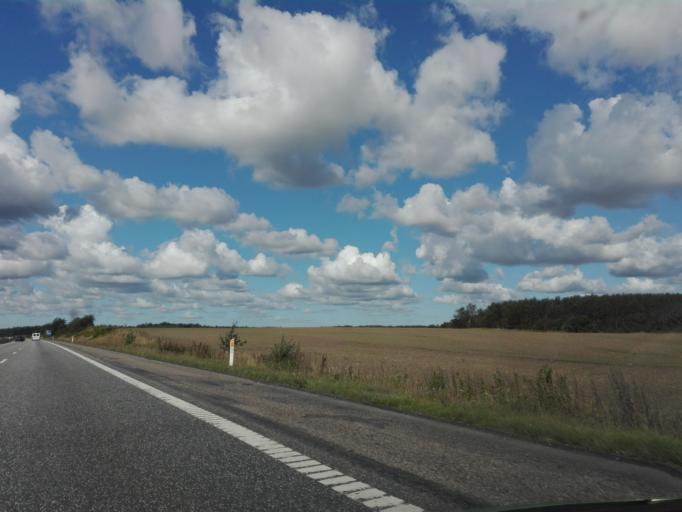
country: DK
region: North Denmark
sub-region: Mariagerfjord Kommune
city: Hobro
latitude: 56.5621
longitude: 9.8638
